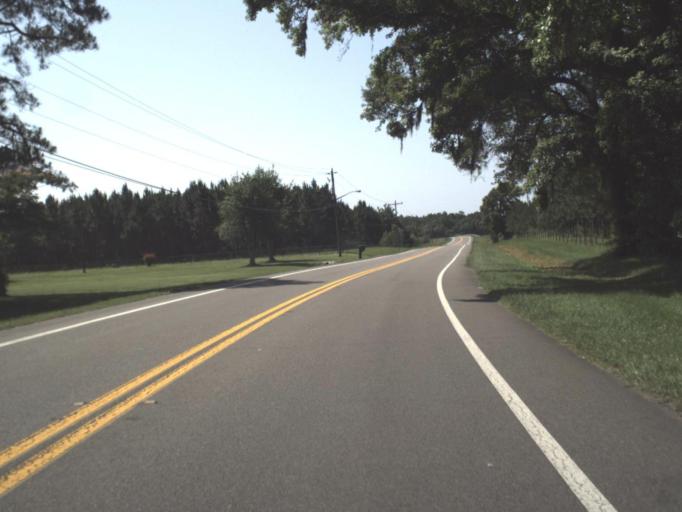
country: US
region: Florida
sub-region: Nassau County
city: Nassau Village-Ratliff
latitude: 30.5159
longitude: -81.7608
